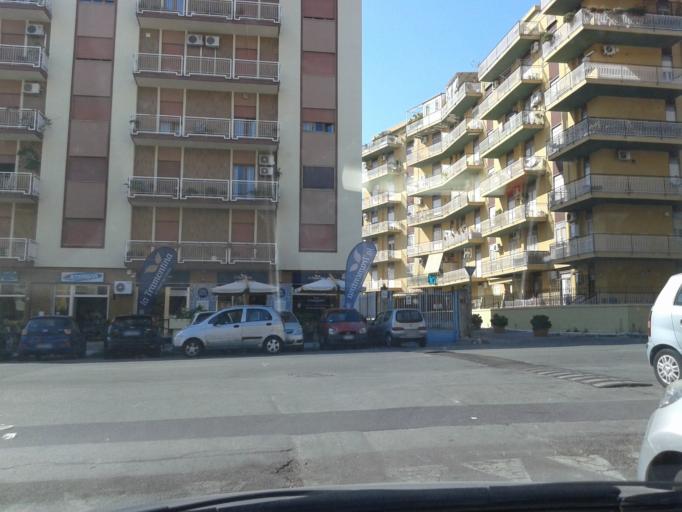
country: IT
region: Sicily
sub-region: Palermo
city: Palermo
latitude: 38.1058
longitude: 13.3324
